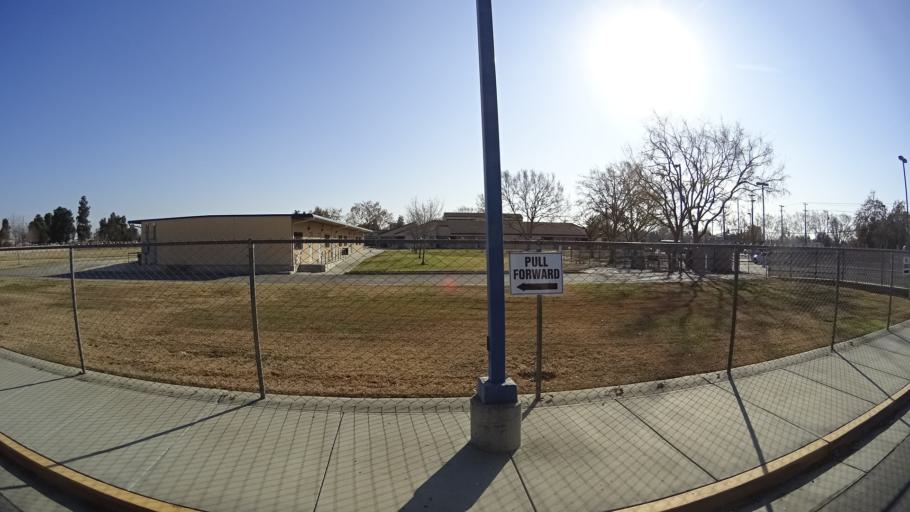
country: US
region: California
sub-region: Kern County
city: Greenacres
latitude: 35.3806
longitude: -119.1089
